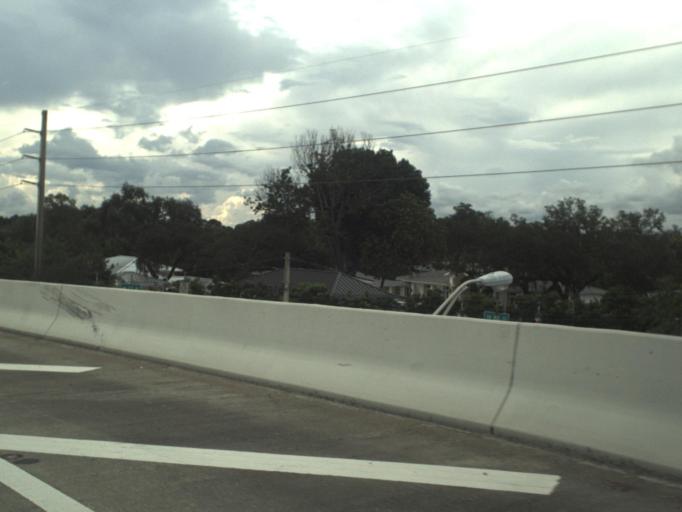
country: US
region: Florida
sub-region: Miami-Dade County
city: Kendall
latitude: 25.6959
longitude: -80.3090
